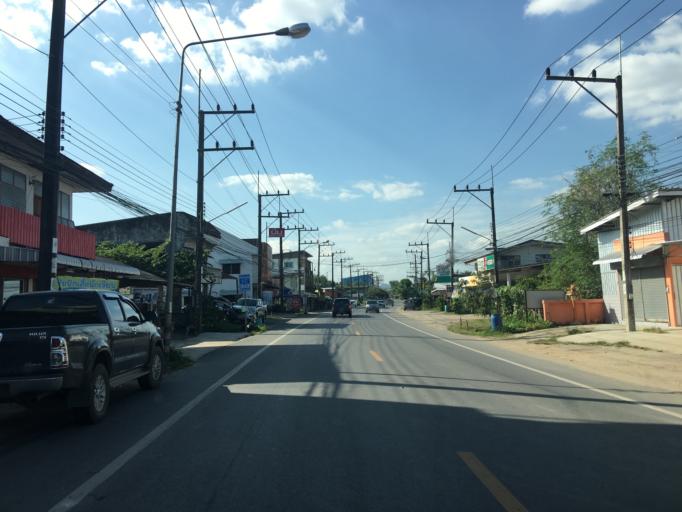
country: TH
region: Phayao
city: Chun
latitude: 19.3420
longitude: 100.1223
